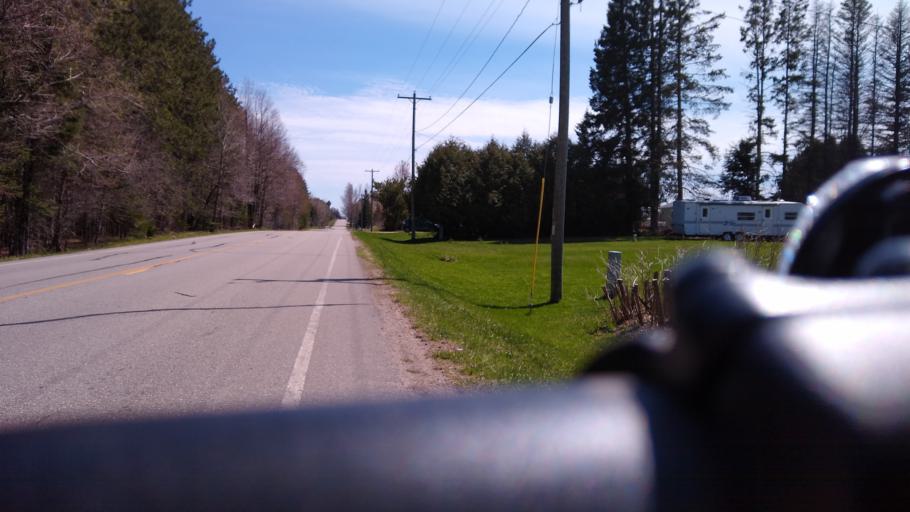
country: US
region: Michigan
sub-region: Delta County
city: Escanaba
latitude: 45.7279
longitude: -87.2025
